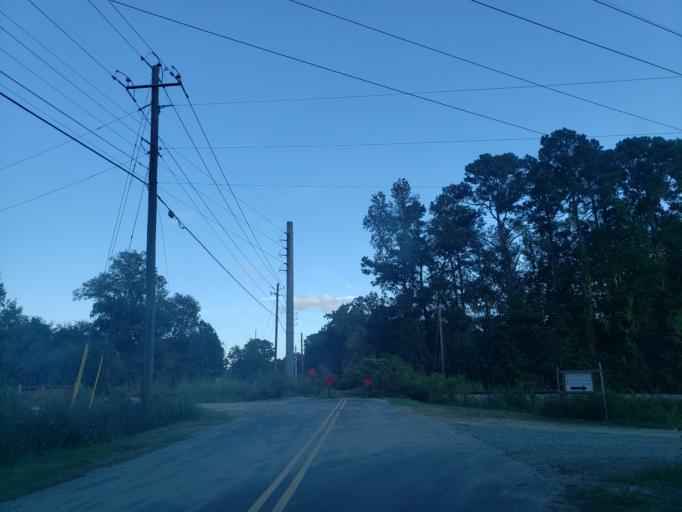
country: US
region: Georgia
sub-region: Chatham County
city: Georgetown
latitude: 31.9919
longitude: -81.2350
